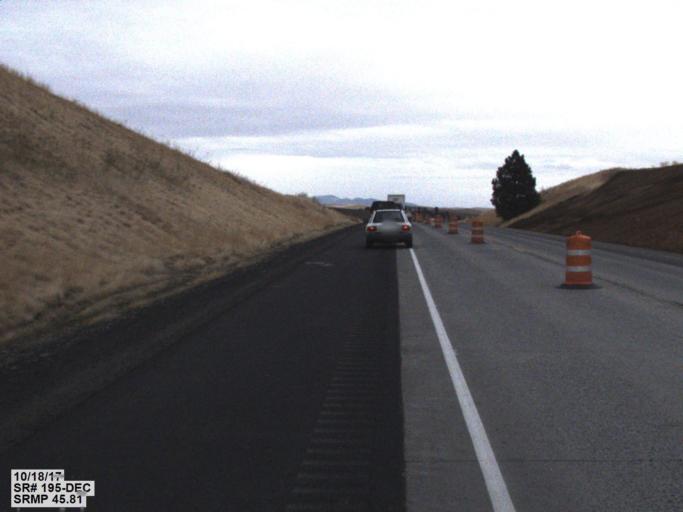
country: US
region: Washington
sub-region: Whitman County
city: Colfax
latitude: 46.9792
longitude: -117.3365
